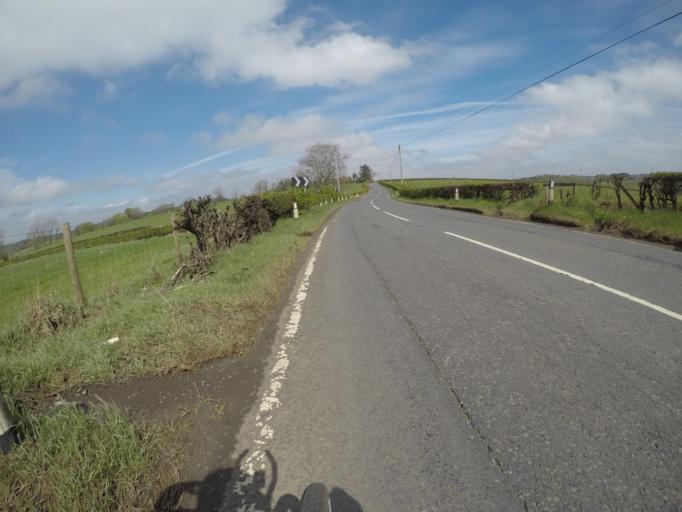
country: GB
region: Scotland
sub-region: East Ayrshire
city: Stewarton
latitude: 55.6901
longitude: -4.4969
